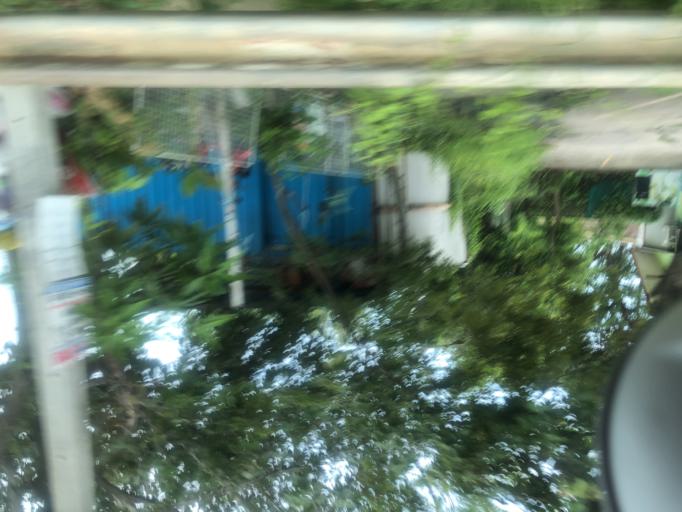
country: TH
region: Bangkok
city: Don Mueang
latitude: 13.9671
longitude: 100.6082
